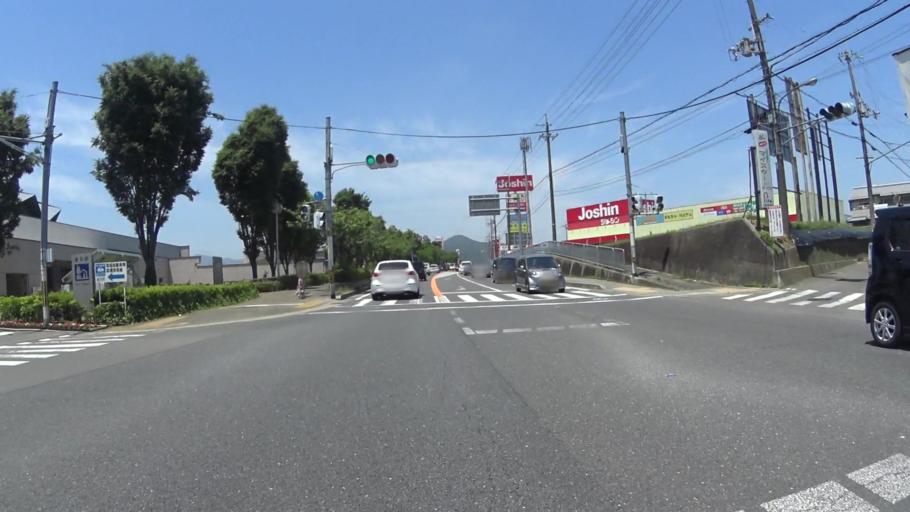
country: JP
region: Kyoto
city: Kameoka
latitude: 35.0153
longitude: 135.5673
